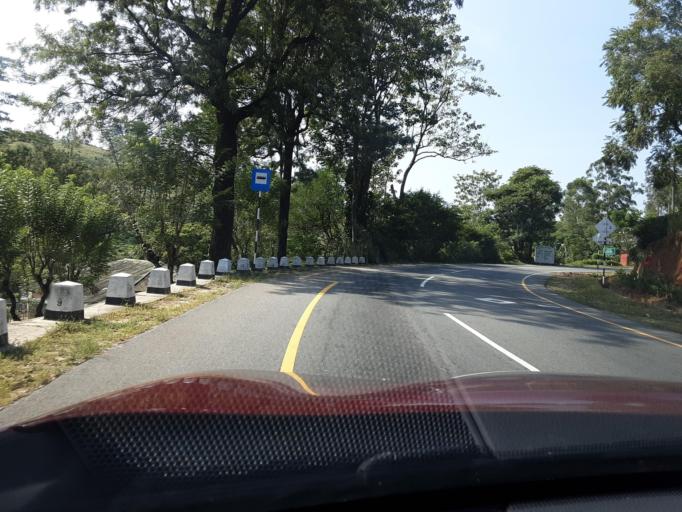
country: LK
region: Uva
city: Badulla
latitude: 6.9571
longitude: 81.1199
